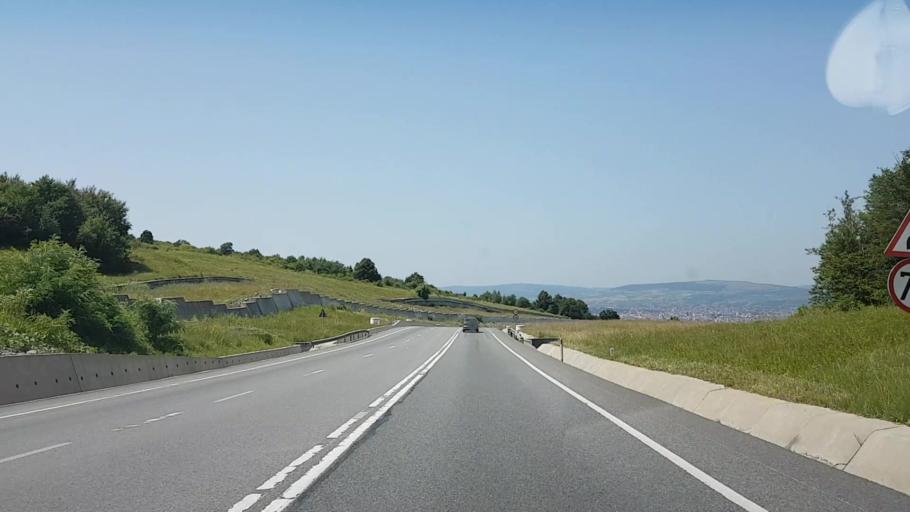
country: RO
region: Cluj
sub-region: Comuna Feleacu
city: Feleacu
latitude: 46.7214
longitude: 23.6490
